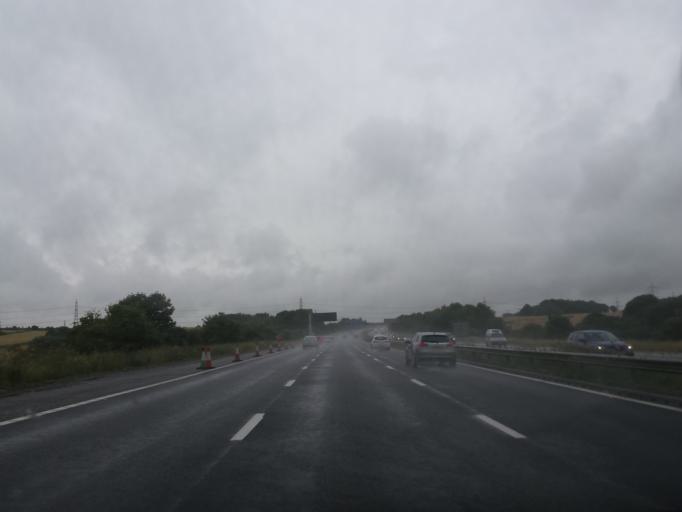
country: GB
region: England
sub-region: Rotherham
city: Bramley
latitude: 53.4131
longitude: -1.2563
